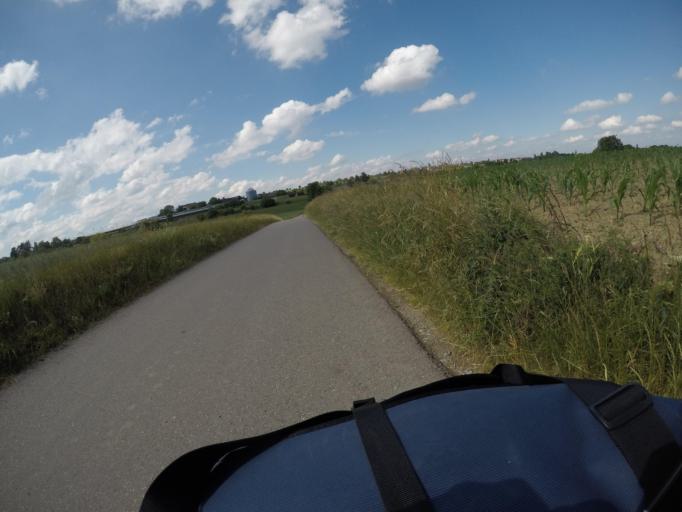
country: DE
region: Baden-Wuerttemberg
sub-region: Regierungsbezirk Stuttgart
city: Herrenberg
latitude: 48.6008
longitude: 8.8338
